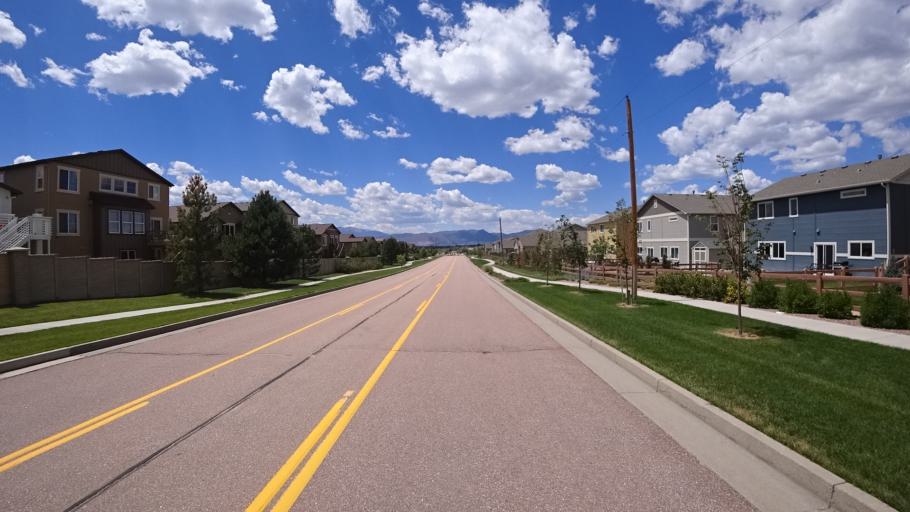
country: US
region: Colorado
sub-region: El Paso County
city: Black Forest
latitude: 38.9514
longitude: -104.7083
